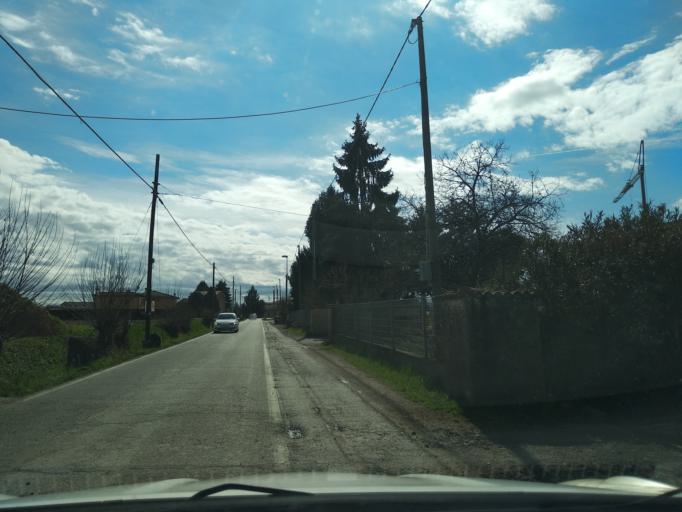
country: IT
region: Veneto
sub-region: Provincia di Vicenza
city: Vigardolo
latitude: 45.6098
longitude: 11.5954
